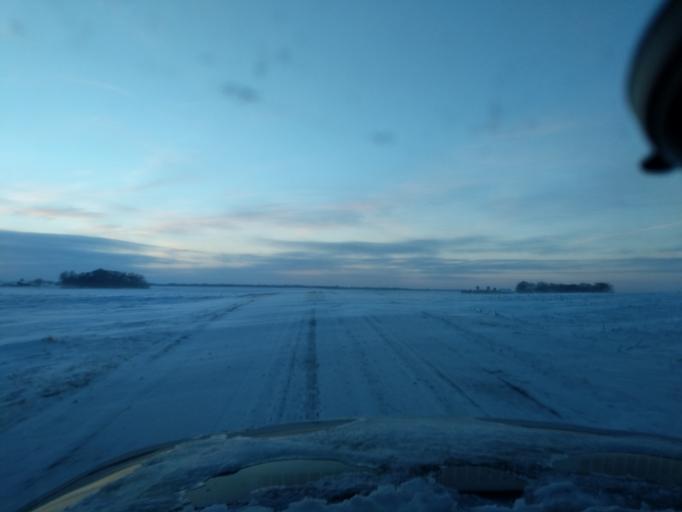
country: US
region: Minnesota
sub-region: Renville County
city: Renville
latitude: 44.7270
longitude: -95.3454
